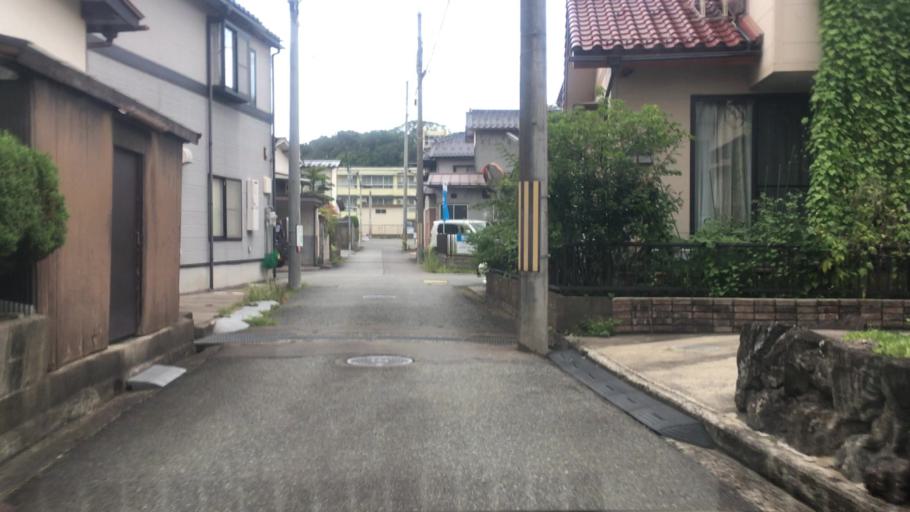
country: JP
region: Hyogo
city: Toyooka
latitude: 35.5361
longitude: 134.8206
